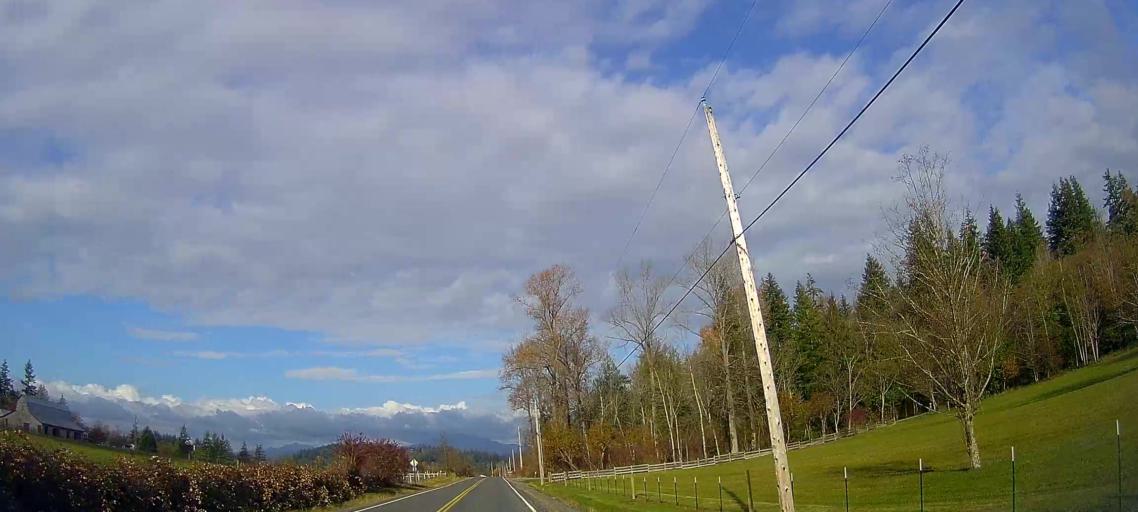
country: US
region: Washington
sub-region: Skagit County
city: Big Lake
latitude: 48.4289
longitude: -122.2420
